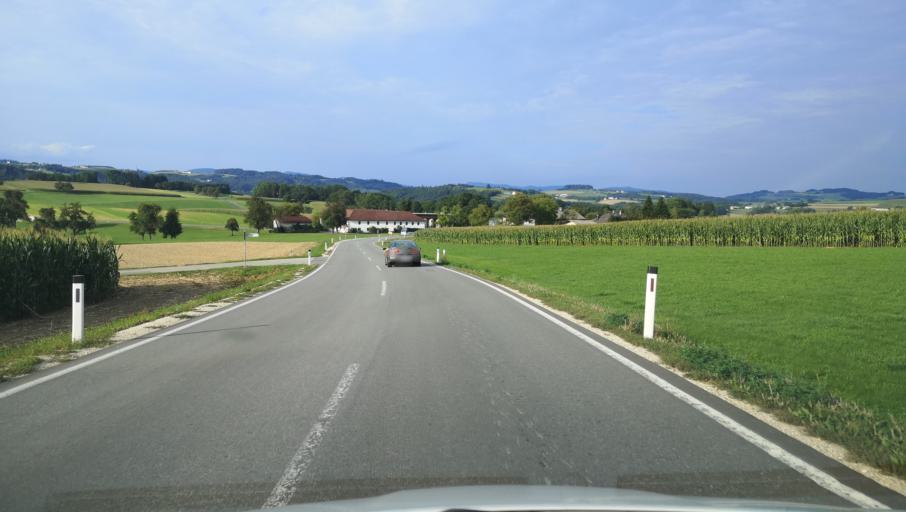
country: AT
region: Lower Austria
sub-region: Politischer Bezirk Amstetten
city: Amstetten
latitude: 48.1579
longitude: 14.9050
